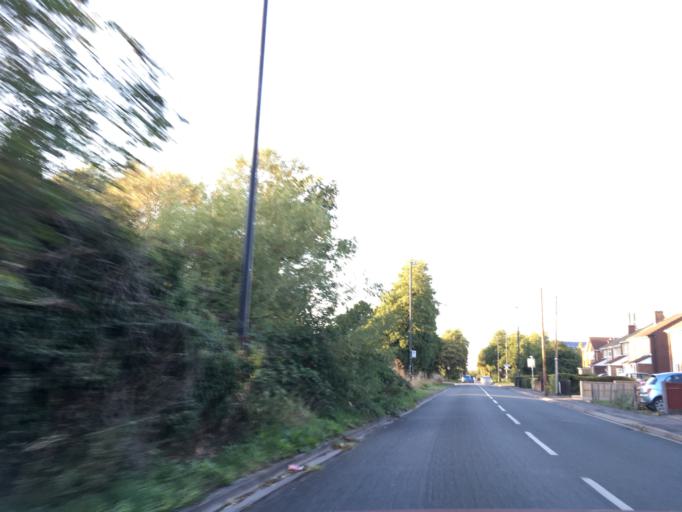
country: GB
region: England
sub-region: Bath and North East Somerset
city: Whitchurch
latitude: 51.4092
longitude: -2.5478
